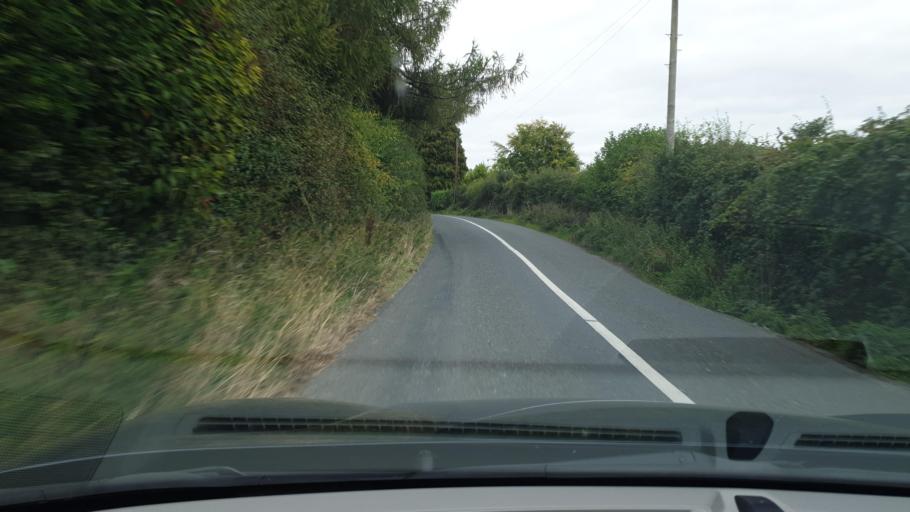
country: IE
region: Leinster
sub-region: Kildare
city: Kilcock
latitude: 53.4304
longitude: -6.6539
